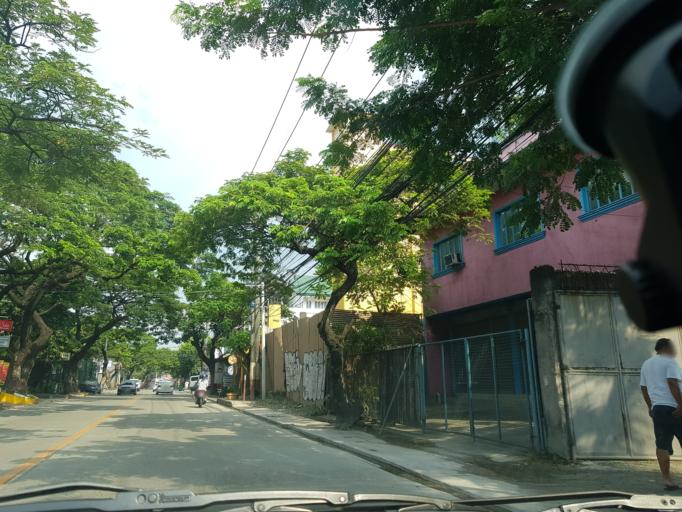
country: PH
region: Calabarzon
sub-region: Province of Rizal
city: Cainta
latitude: 14.5753
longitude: 121.0915
